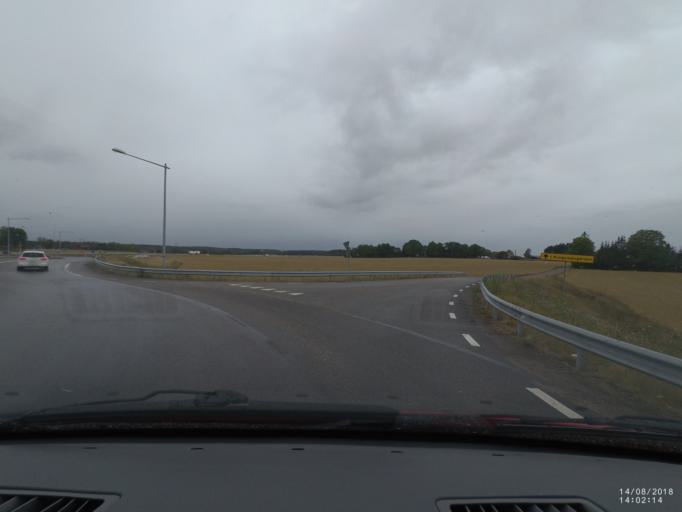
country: SE
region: Soedermanland
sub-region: Nykopings Kommun
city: Nykoping
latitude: 58.7512
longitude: 16.9711
